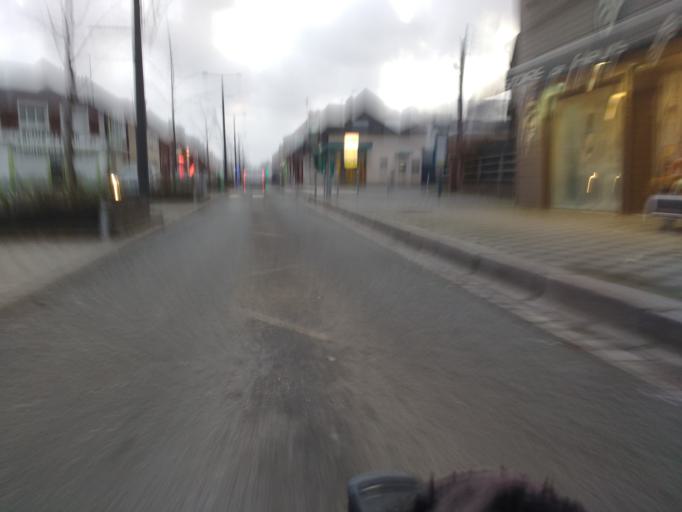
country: FR
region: Picardie
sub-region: Departement de la Somme
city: Longueau
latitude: 49.8729
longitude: 2.3514
